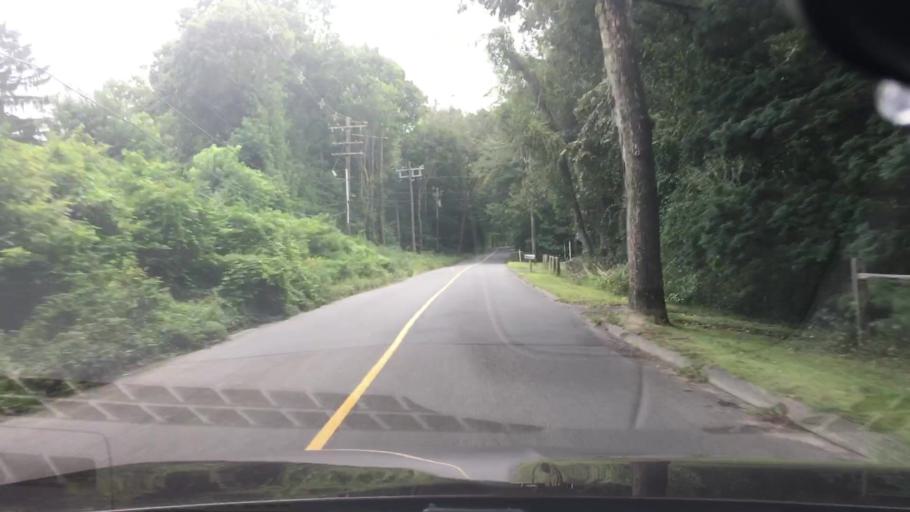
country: US
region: Connecticut
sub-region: New Haven County
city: Madison
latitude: 41.3504
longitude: -72.5624
